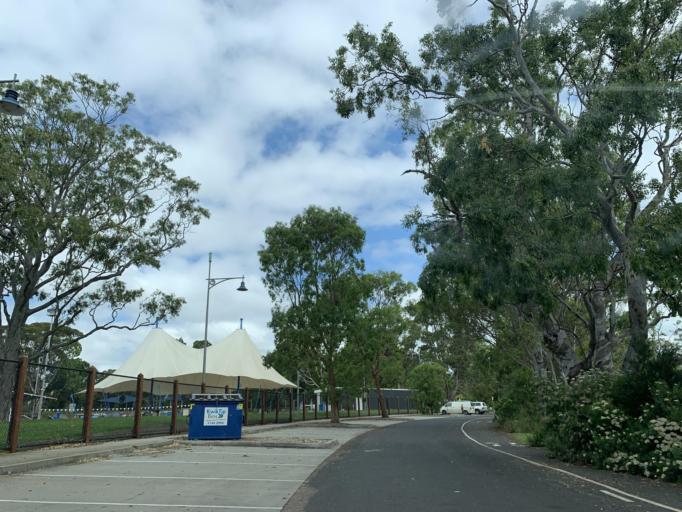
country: AU
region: Victoria
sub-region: Wellington
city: Sale
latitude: -38.1121
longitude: 147.0793
